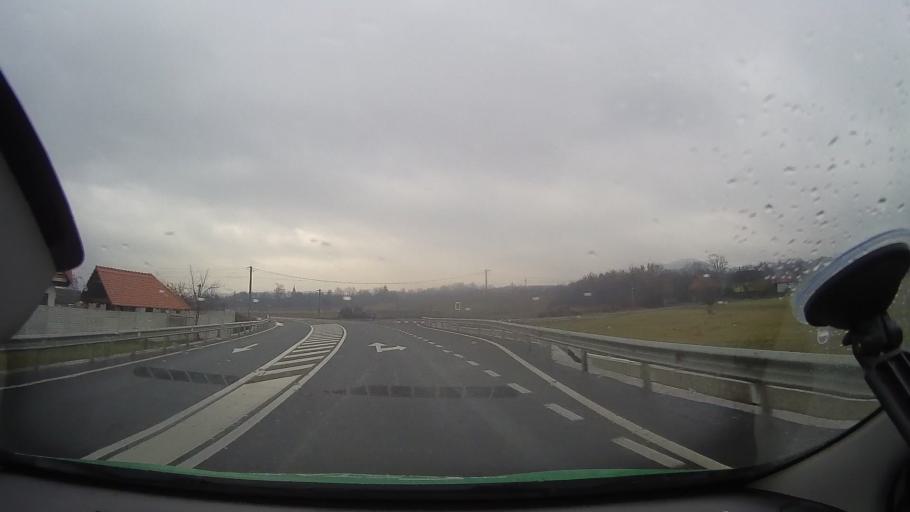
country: RO
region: Hunedoara
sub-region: Comuna Baia de Cris
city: Baia de Cris
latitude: 46.1742
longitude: 22.7090
